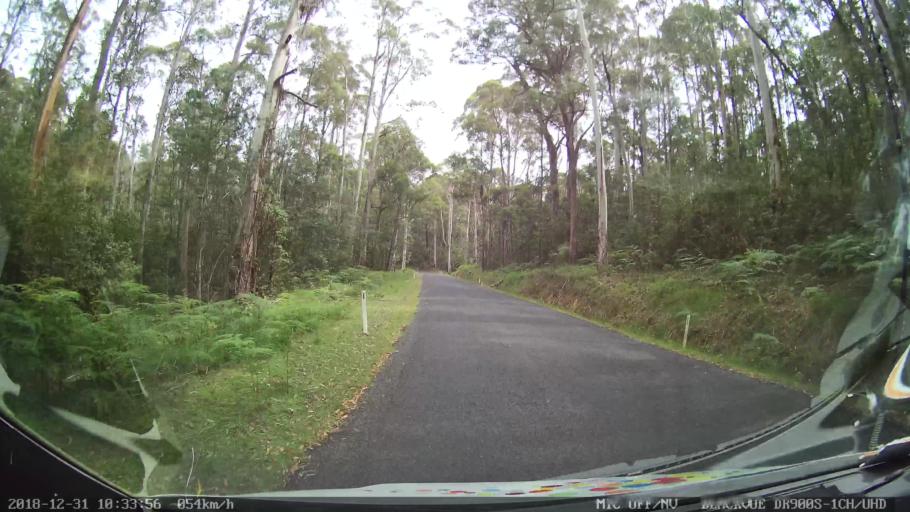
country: AU
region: New South Wales
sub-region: Snowy River
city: Jindabyne
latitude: -36.4439
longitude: 148.1673
